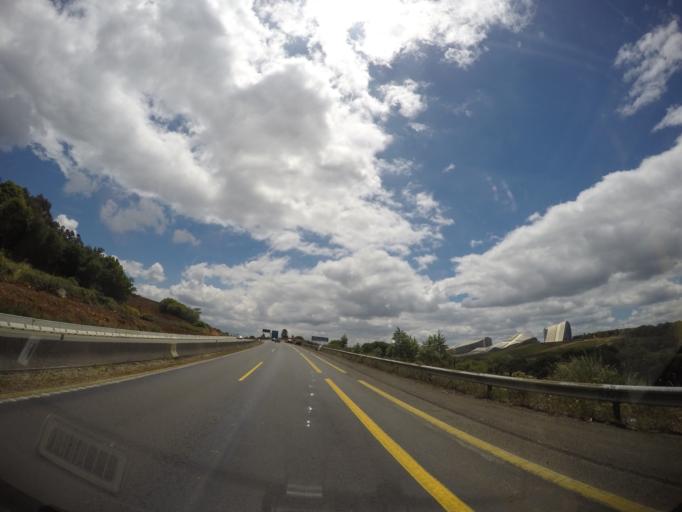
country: ES
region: Galicia
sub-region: Provincia da Coruna
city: Negreira
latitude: 42.8374
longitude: -8.7233
